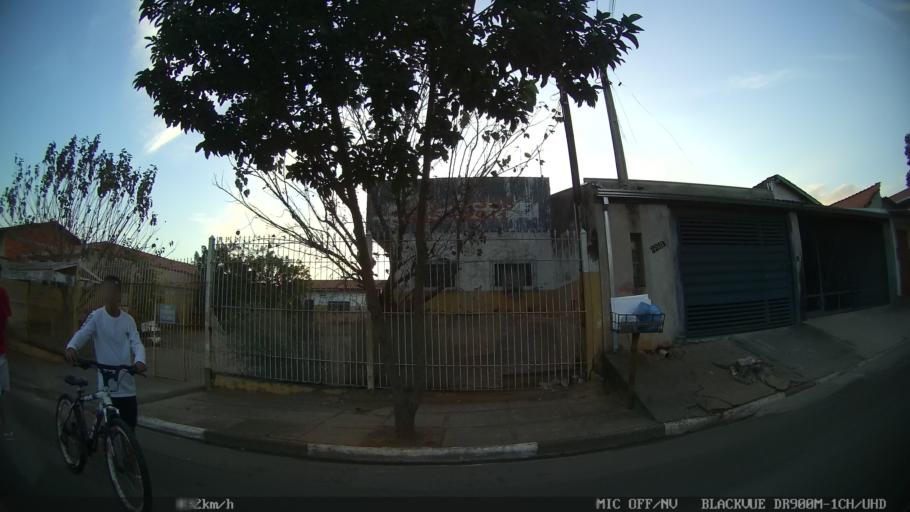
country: BR
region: Sao Paulo
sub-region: Hortolandia
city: Hortolandia
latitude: -22.8579
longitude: -47.2140
